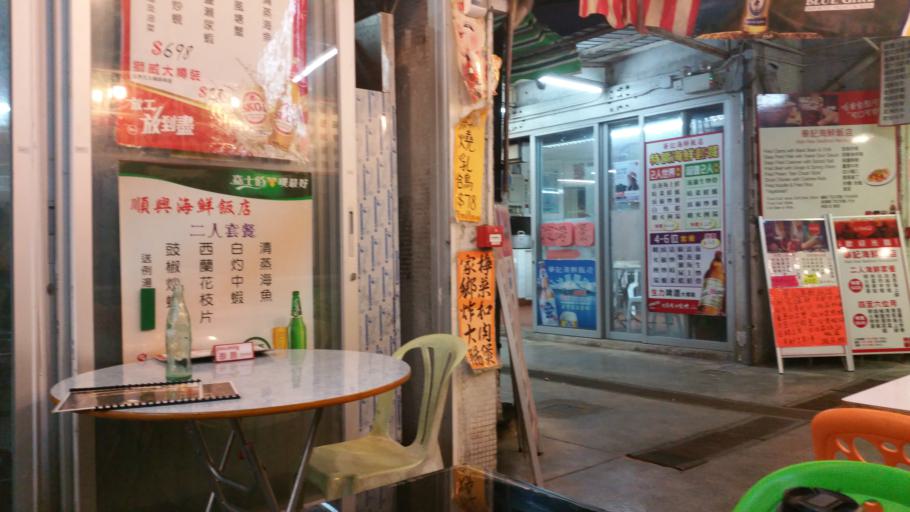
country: HK
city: Yung Shue Wan
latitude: 22.2662
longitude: 114.0013
